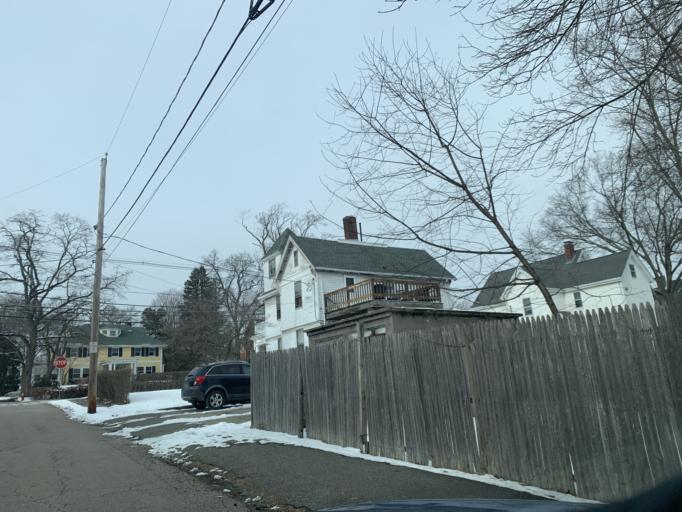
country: US
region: Massachusetts
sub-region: Norfolk County
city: Norwood
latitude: 42.1892
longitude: -71.2064
